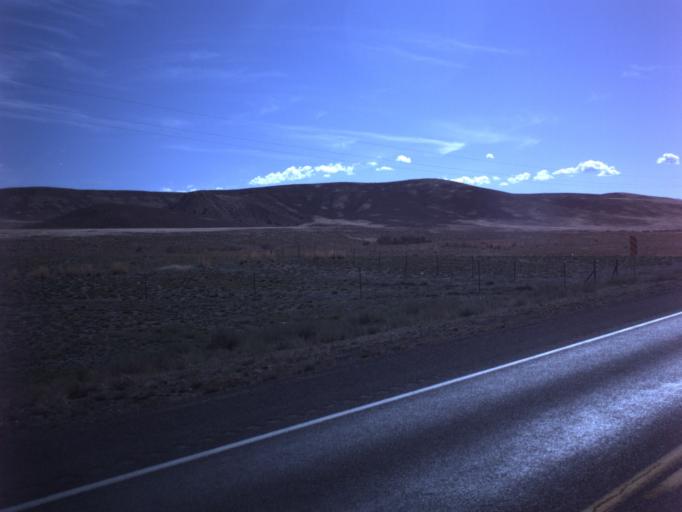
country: US
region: Utah
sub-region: Sanpete County
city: Gunnison
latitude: 39.1967
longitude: -111.8449
